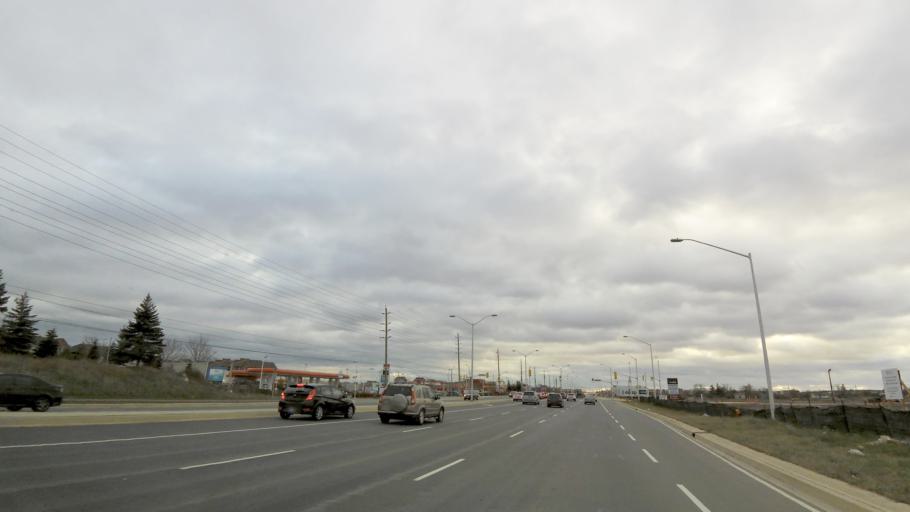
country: CA
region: Ontario
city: Oakville
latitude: 43.4918
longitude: -79.7160
